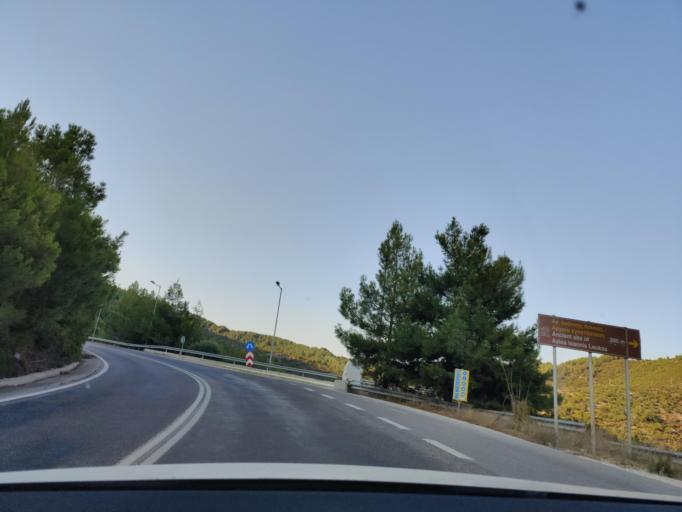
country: GR
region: East Macedonia and Thrace
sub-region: Nomos Kavalas
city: Potamia
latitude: 40.6175
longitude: 24.7583
